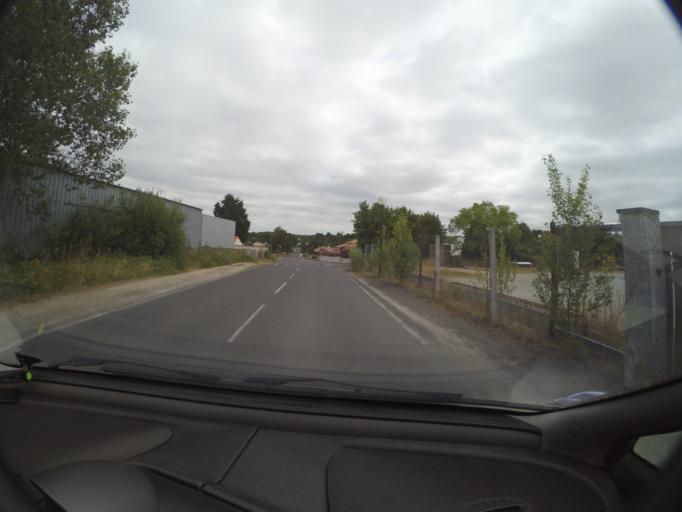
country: FR
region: Pays de la Loire
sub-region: Departement de la Vendee
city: Saint-Hilaire-de-Loulay
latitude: 47.0016
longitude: -1.3385
